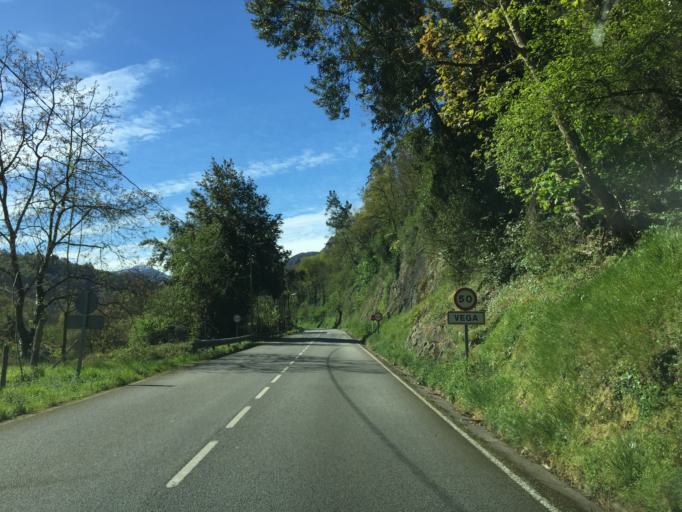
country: ES
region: Asturias
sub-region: Province of Asturias
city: Proaza
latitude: 43.3335
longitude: -5.9874
